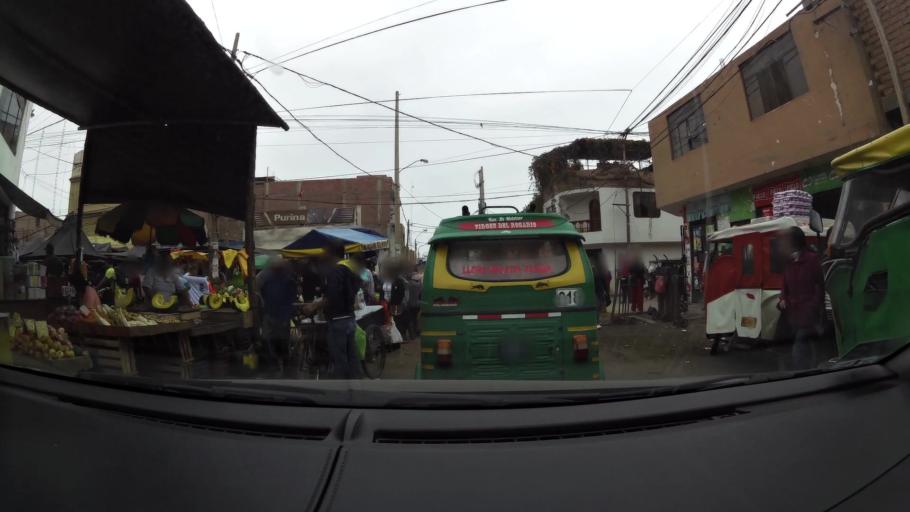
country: PE
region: Lima
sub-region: Provincia de Huaral
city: Chancay
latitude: -11.5652
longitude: -77.2710
